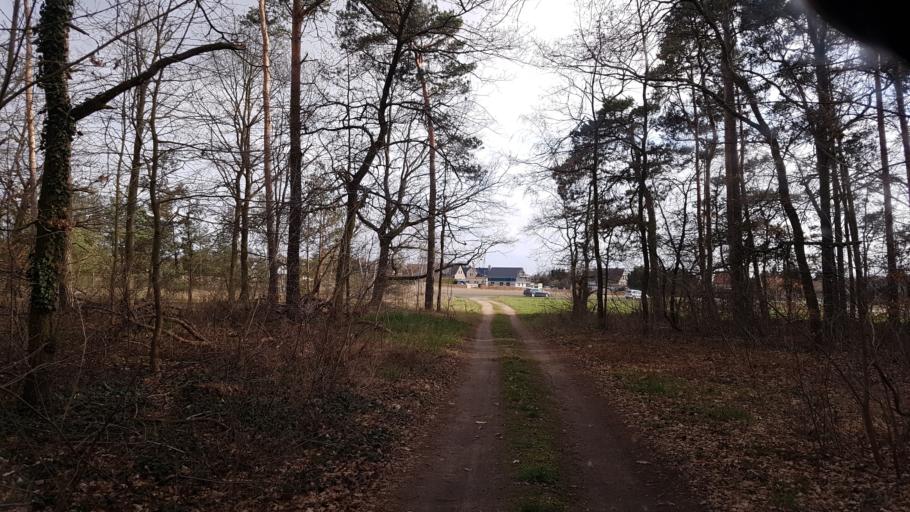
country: DE
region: Brandenburg
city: Bad Liebenwerda
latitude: 51.5361
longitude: 13.4415
